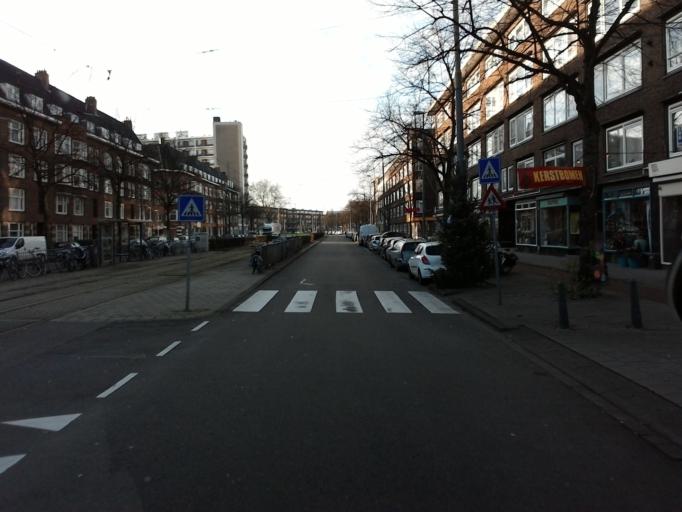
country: NL
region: South Holland
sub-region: Gemeente Rotterdam
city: Rotterdam
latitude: 51.9335
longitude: 4.4645
